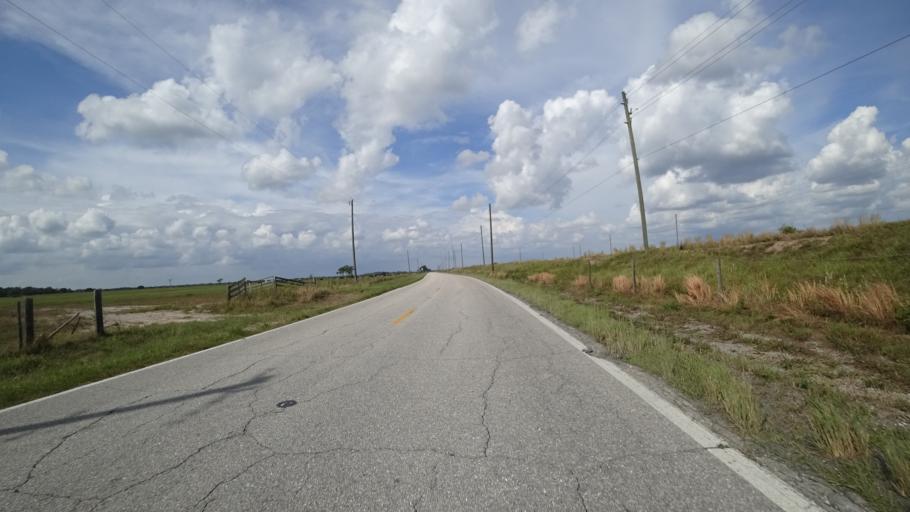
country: US
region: Florida
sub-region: Hardee County
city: Wauchula
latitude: 27.5192
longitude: -82.0729
